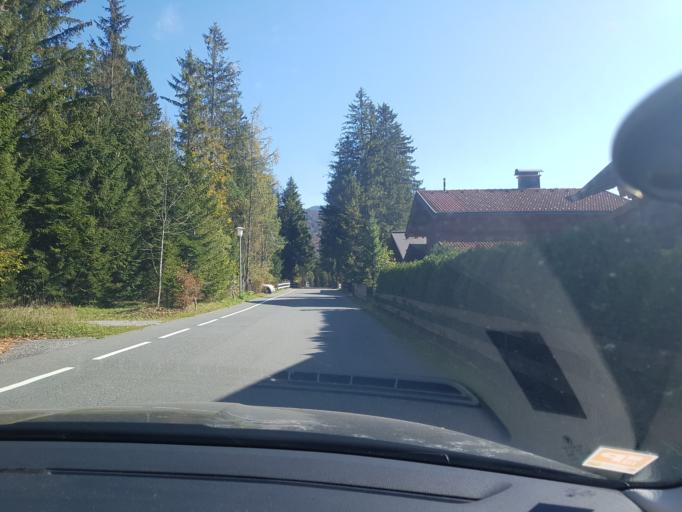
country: AT
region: Tyrol
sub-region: Politischer Bezirk Kitzbuhel
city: Fieberbrunn
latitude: 47.5208
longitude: 12.5810
